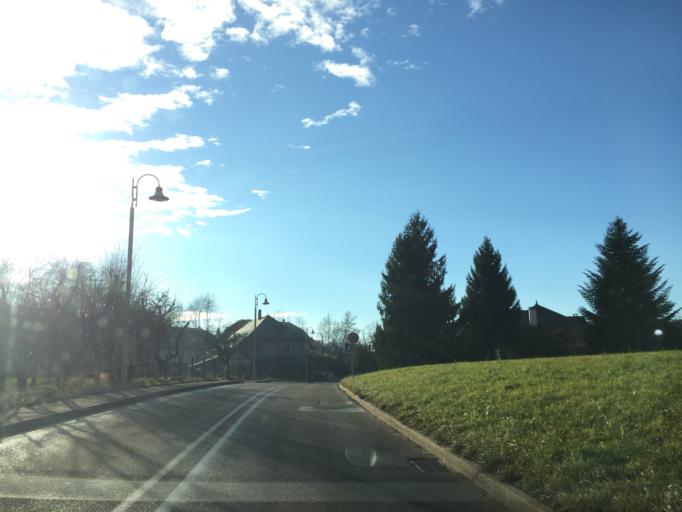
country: FR
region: Rhone-Alpes
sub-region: Departement de la Haute-Savoie
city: Cusy
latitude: 45.7624
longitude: 6.0263
